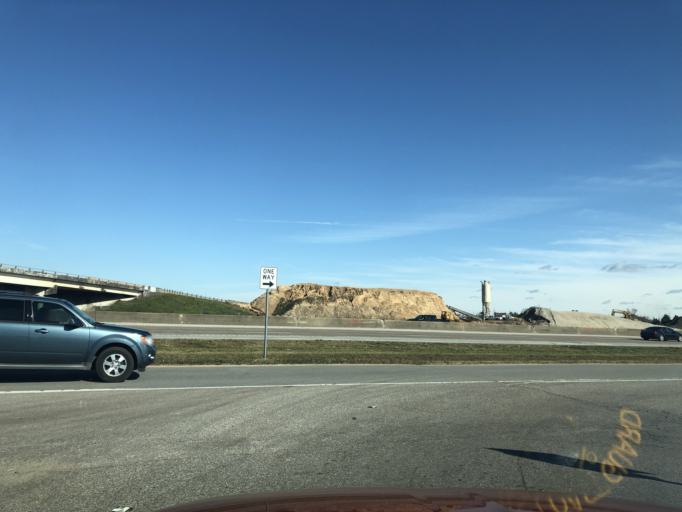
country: US
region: Texas
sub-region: Galveston County
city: Dickinson
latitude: 29.4298
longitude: -95.0604
